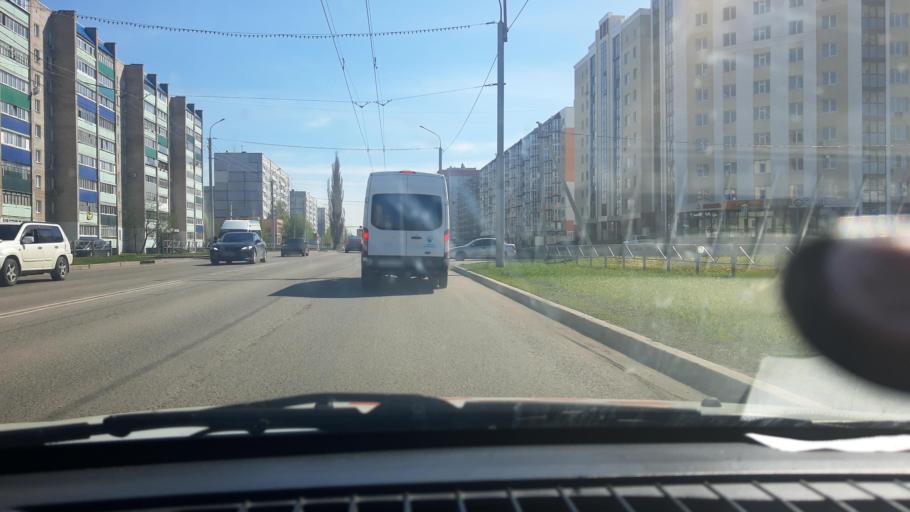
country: RU
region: Bashkortostan
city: Sterlitamak
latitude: 53.6296
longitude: 55.9036
